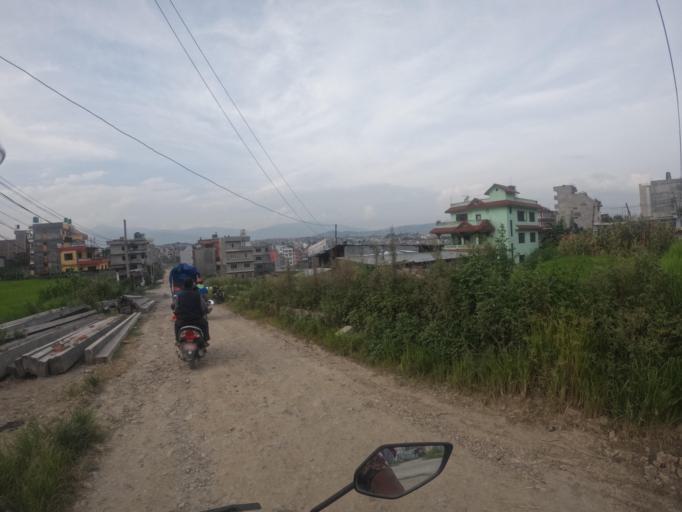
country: NP
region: Central Region
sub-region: Bagmati Zone
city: Bhaktapur
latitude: 27.6788
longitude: 85.3936
